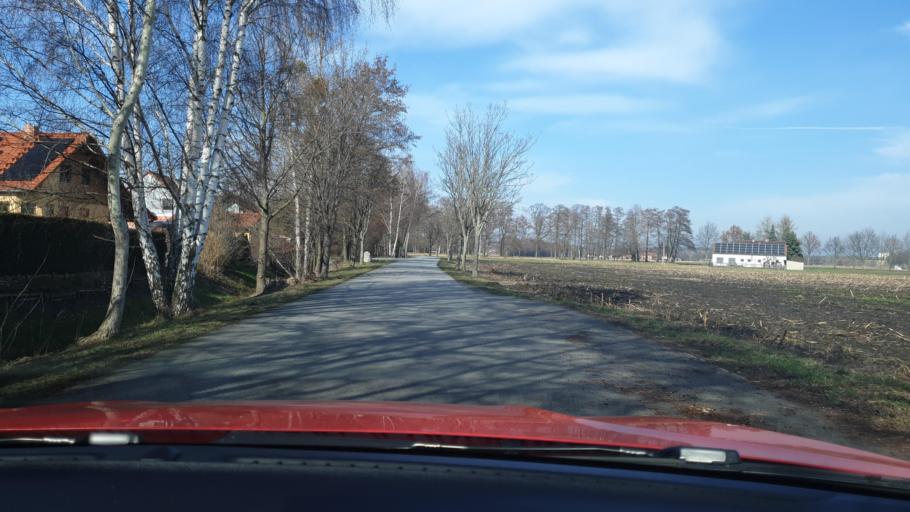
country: DE
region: Saxony
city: Ossling
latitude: 51.4306
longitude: 14.1459
